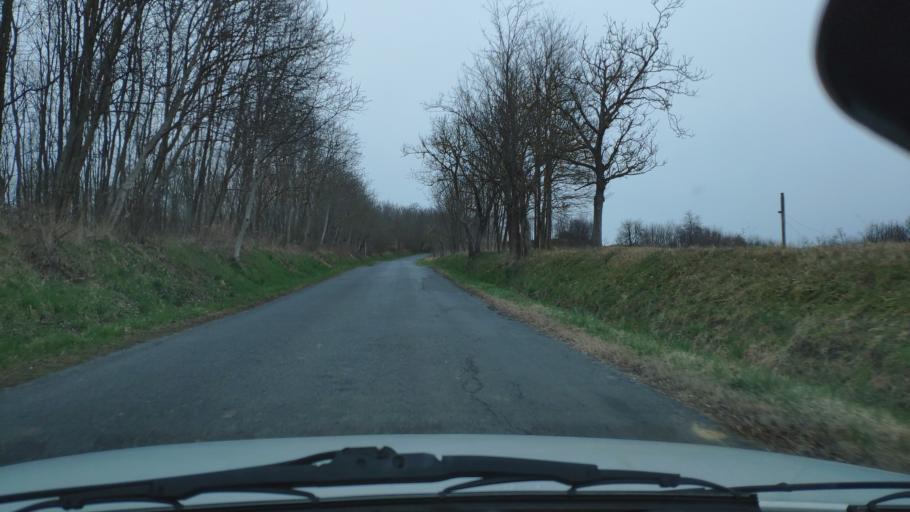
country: HU
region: Zala
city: Pacsa
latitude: 46.6880
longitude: 17.0495
